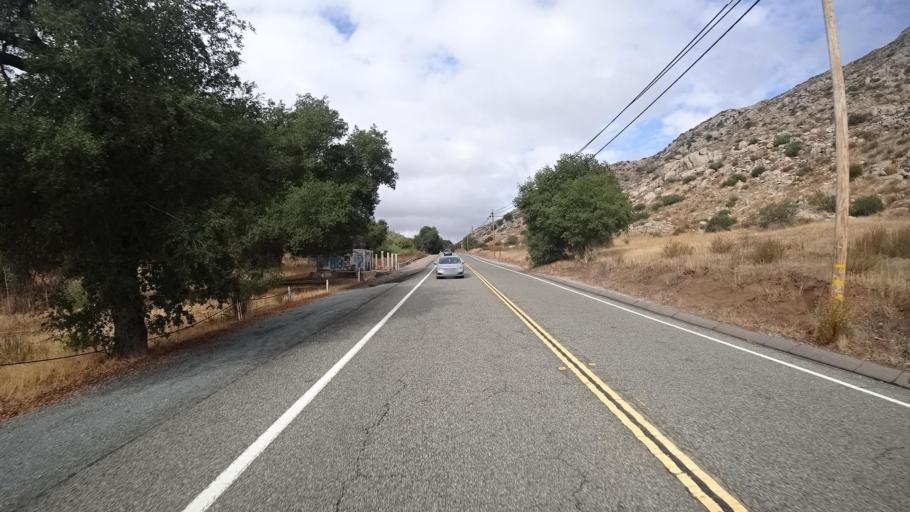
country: MX
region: Baja California
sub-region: Tecate
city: Hacienda Tecate
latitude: 32.5957
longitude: -116.5367
